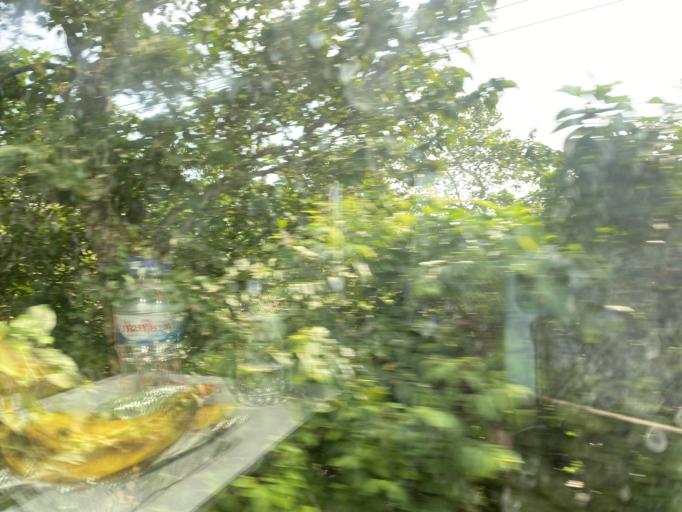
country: BD
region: Chittagong
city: Nabinagar
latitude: 23.9550
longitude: 91.1197
